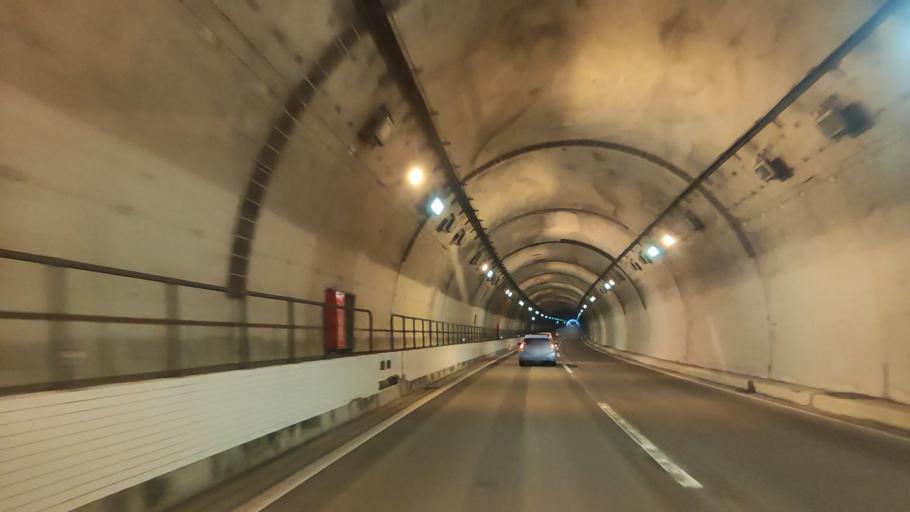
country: JP
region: Ehime
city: Saijo
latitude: 33.8755
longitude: 133.0783
